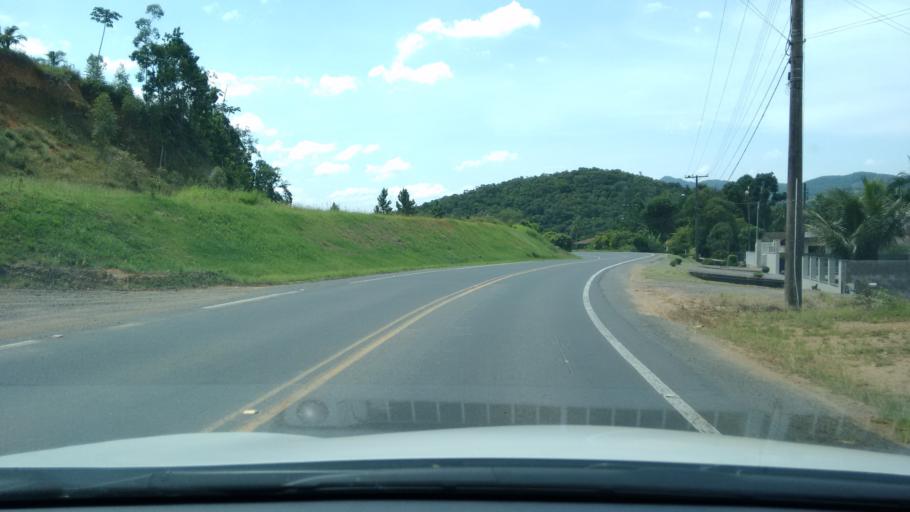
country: BR
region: Santa Catarina
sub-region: Rodeio
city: Gavea
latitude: -26.8866
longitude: -49.3487
